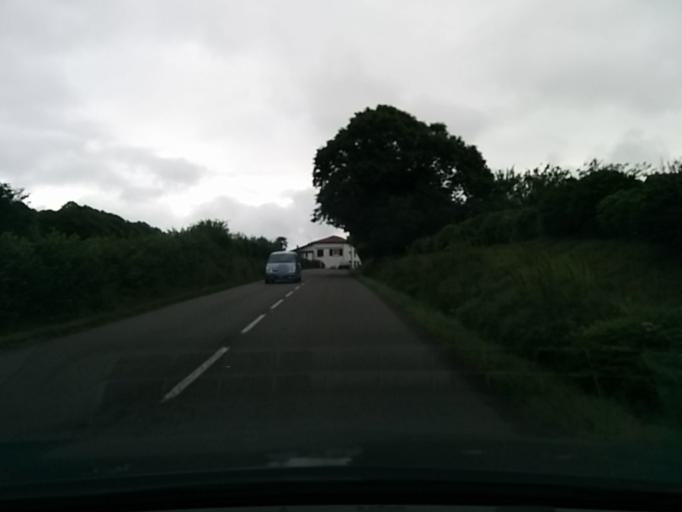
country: FR
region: Aquitaine
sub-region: Departement des Pyrenees-Atlantiques
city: Saint-Pee-sur-Nivelle
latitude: 43.3440
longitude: -1.5499
